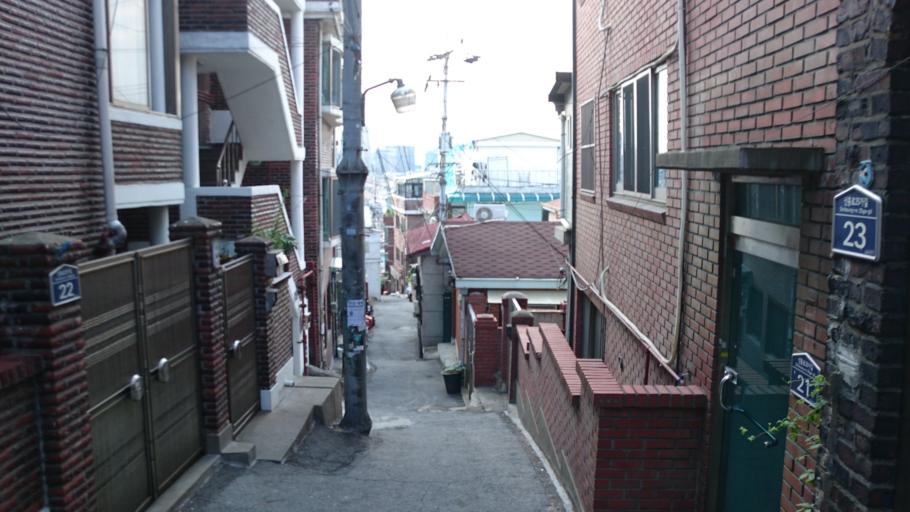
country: KR
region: Seoul
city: Seoul
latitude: 37.5436
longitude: 126.9838
